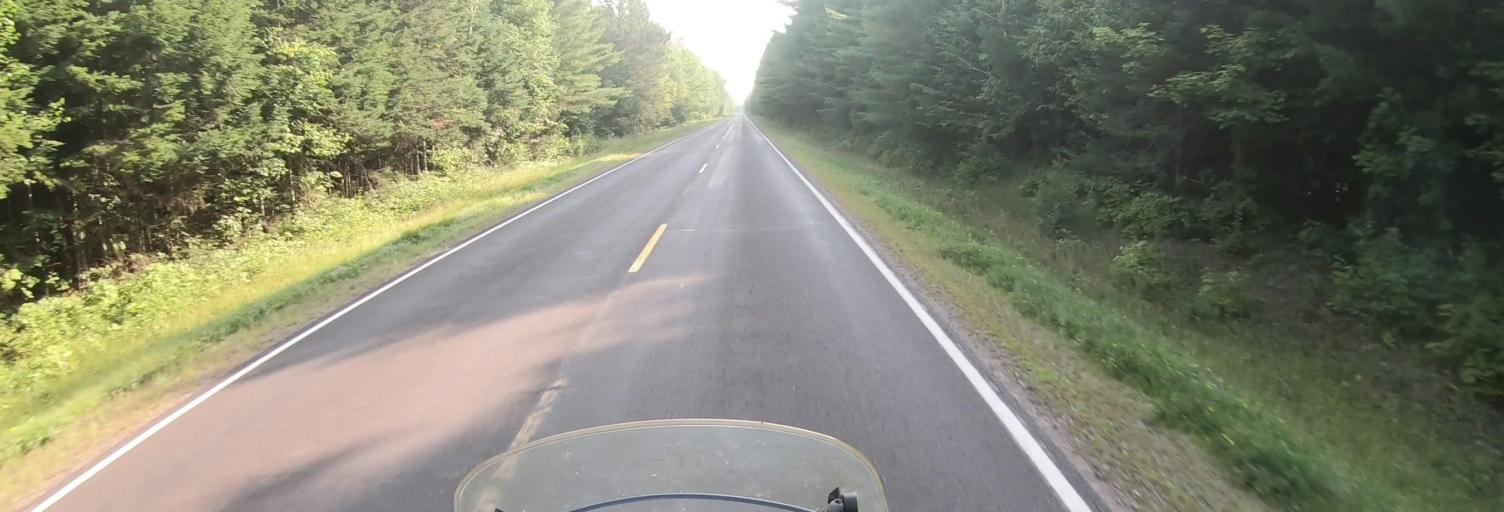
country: US
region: Wisconsin
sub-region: Ashland County
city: Ashland
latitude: 46.1941
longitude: -90.8745
